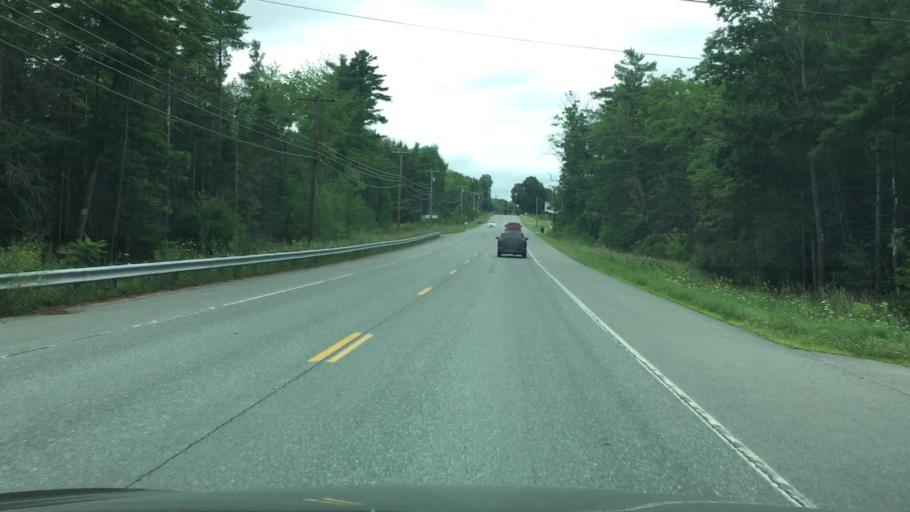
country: US
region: Maine
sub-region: Penobscot County
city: Orrington
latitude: 44.7077
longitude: -68.8242
